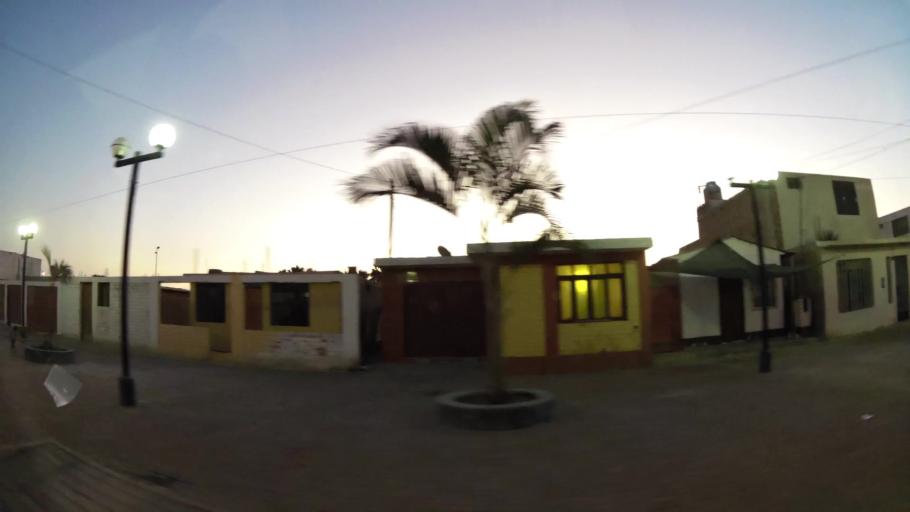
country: PE
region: Ica
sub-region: Provincia de Pisco
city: Pisco
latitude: -13.7153
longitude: -76.2193
